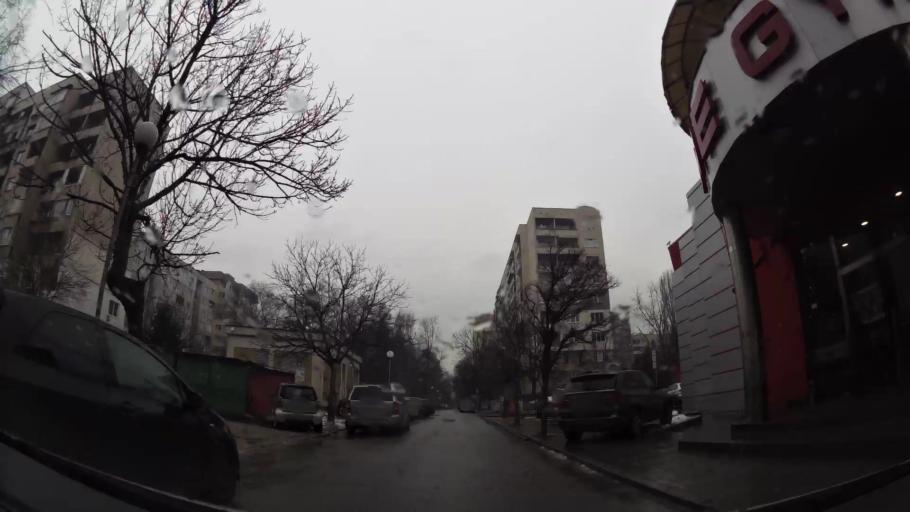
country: BG
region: Sofia-Capital
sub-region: Stolichna Obshtina
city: Sofia
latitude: 42.6705
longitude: 23.2989
